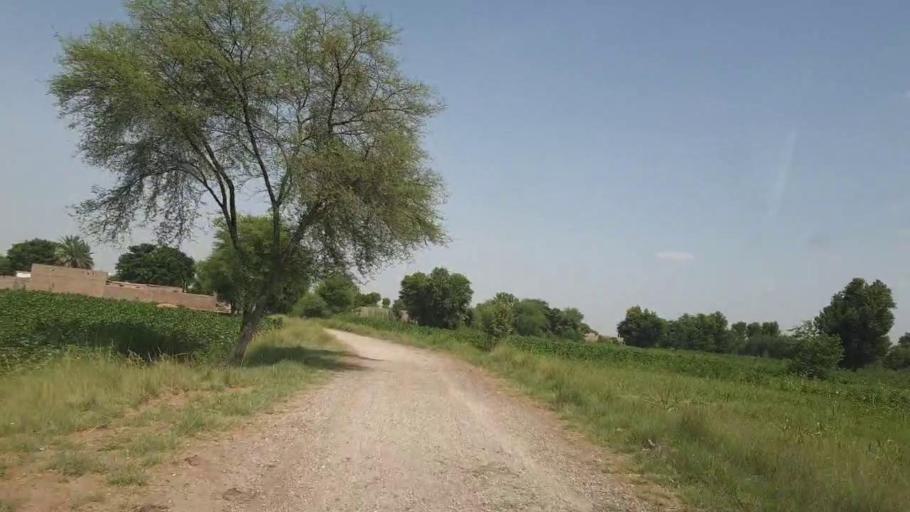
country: PK
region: Sindh
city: Bozdar
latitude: 27.0877
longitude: 68.6032
